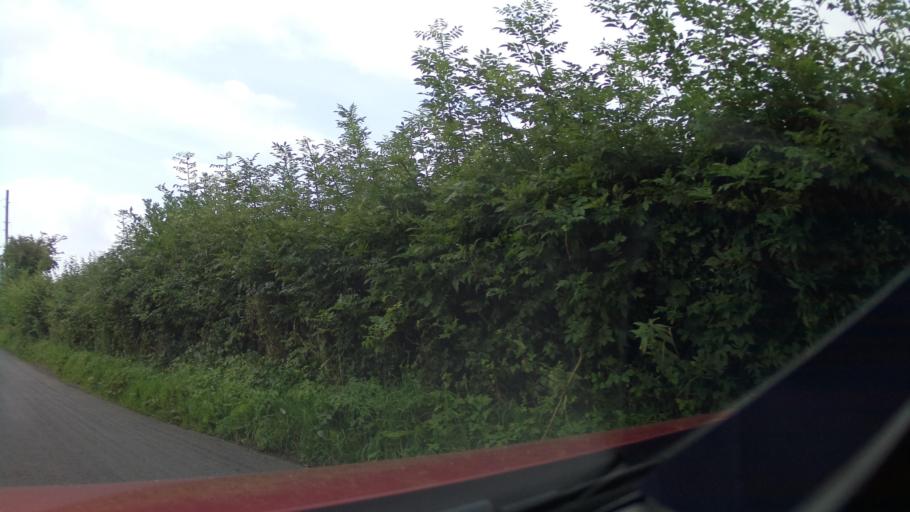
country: GB
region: England
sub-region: Somerset
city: Evercreech
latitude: 51.1695
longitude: -2.5063
